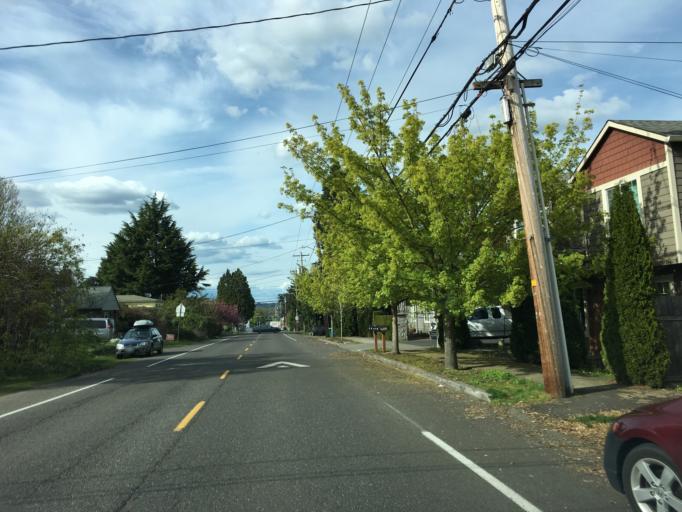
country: US
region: Oregon
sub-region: Multnomah County
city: Lents
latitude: 45.5563
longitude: -122.5547
